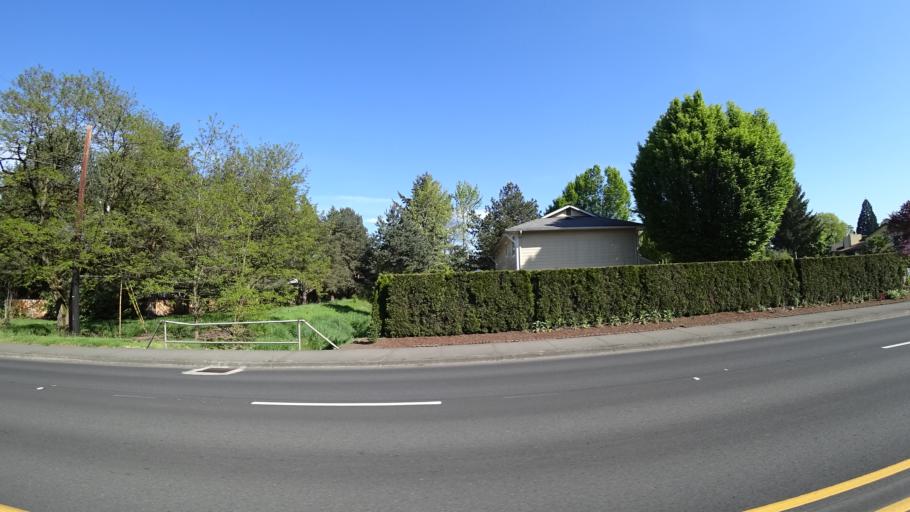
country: US
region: Oregon
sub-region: Washington County
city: Hillsboro
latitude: 45.5257
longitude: -122.9704
